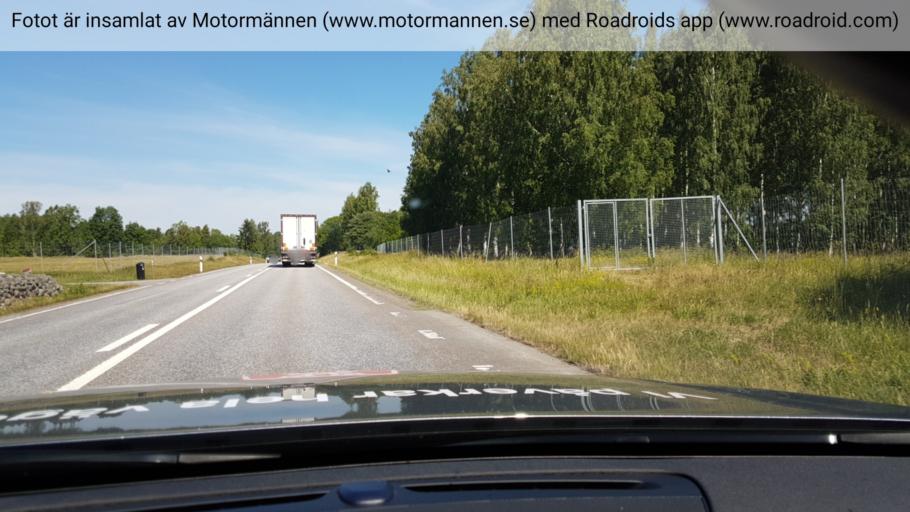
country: SE
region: OErebro
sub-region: Hallsbergs Kommun
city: Palsboda
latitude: 58.9650
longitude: 15.4116
